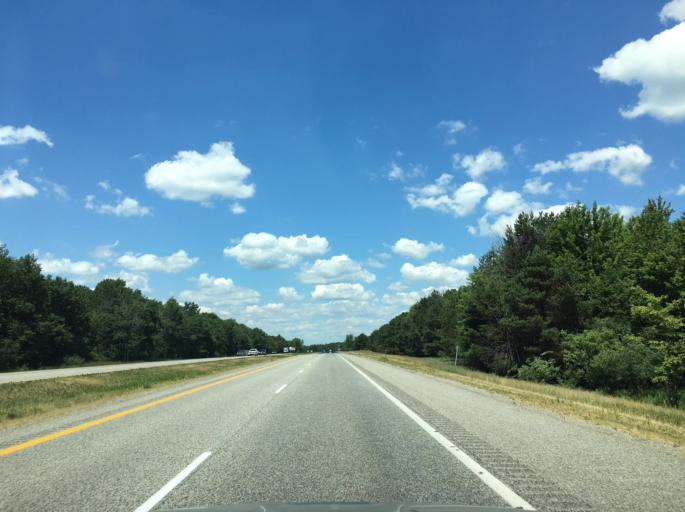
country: US
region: Michigan
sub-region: Midland County
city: Midland
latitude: 43.6496
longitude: -84.1982
